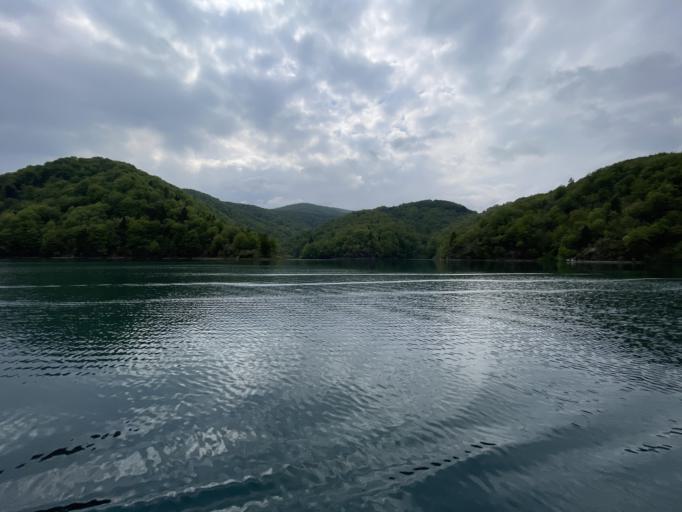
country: HR
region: Licko-Senjska
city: Jezerce
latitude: 44.8923
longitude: 15.6043
